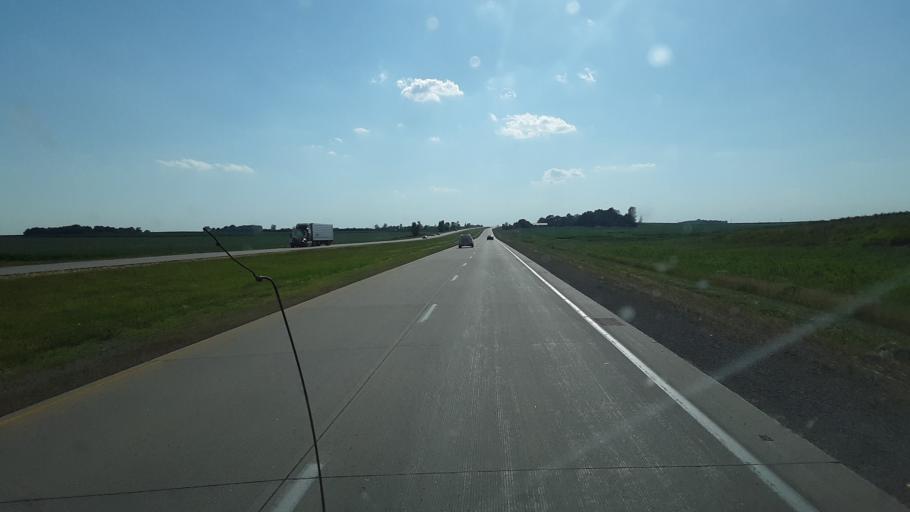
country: US
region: Iowa
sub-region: Grundy County
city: Dike
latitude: 42.4634
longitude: -92.7186
